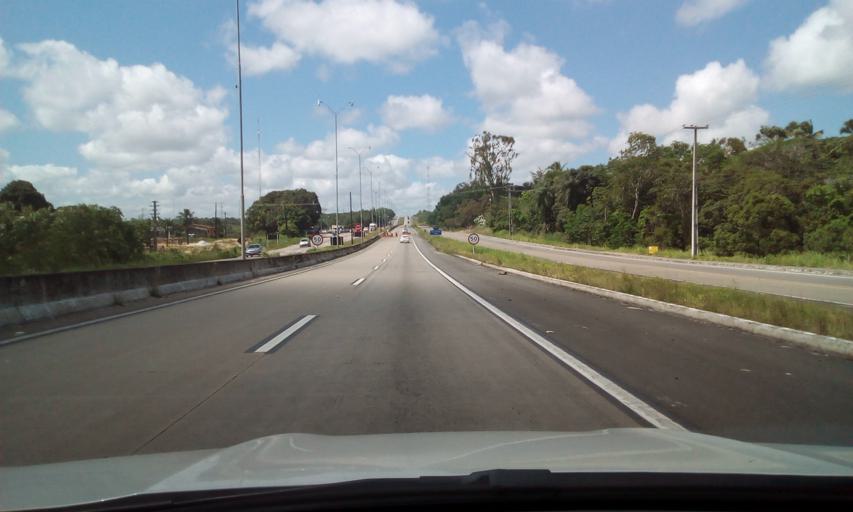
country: BR
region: Paraiba
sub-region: Conde
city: Conde
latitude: -7.3365
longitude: -34.9475
